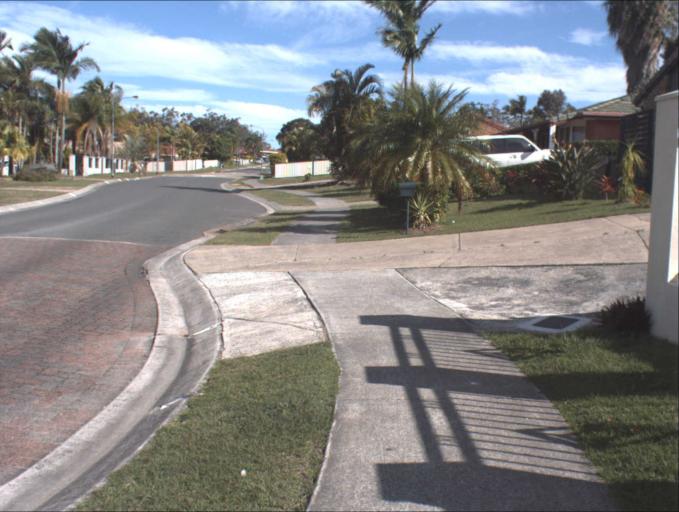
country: AU
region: Queensland
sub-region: Logan
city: Logan Reserve
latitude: -27.6942
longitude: 153.0807
